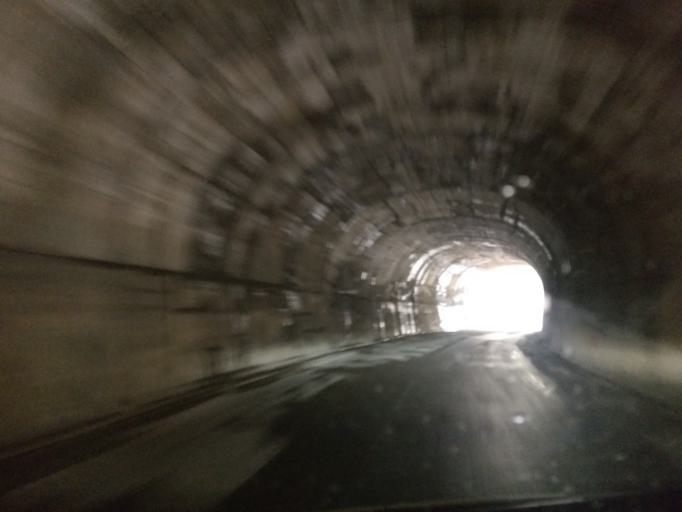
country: ME
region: Opstina Pluzine
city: Pluzine
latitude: 43.2429
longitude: 18.8406
